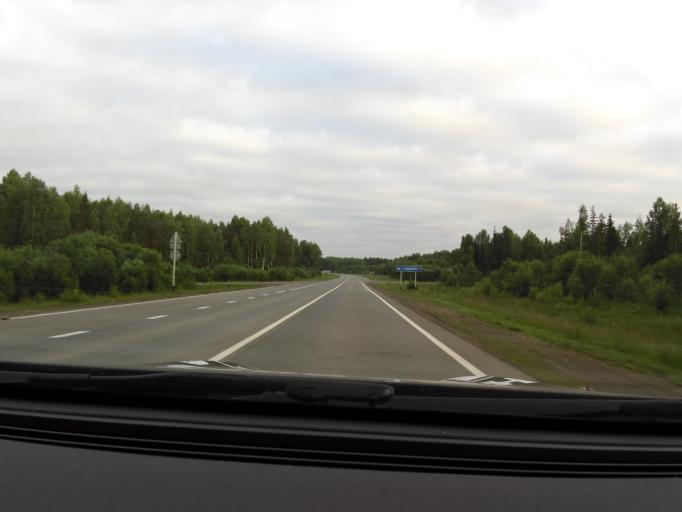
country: RU
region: Perm
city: Siva
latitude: 58.4412
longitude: 54.4310
